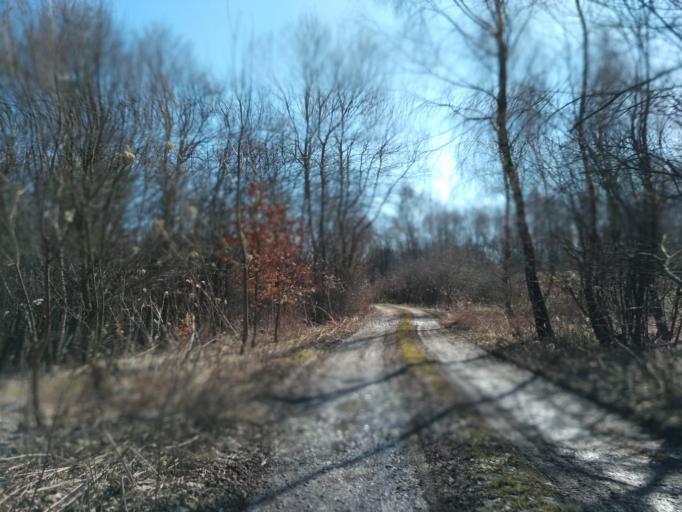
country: PL
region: Subcarpathian Voivodeship
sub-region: Powiat brzozowski
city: Blizne
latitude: 49.7624
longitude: 21.9902
